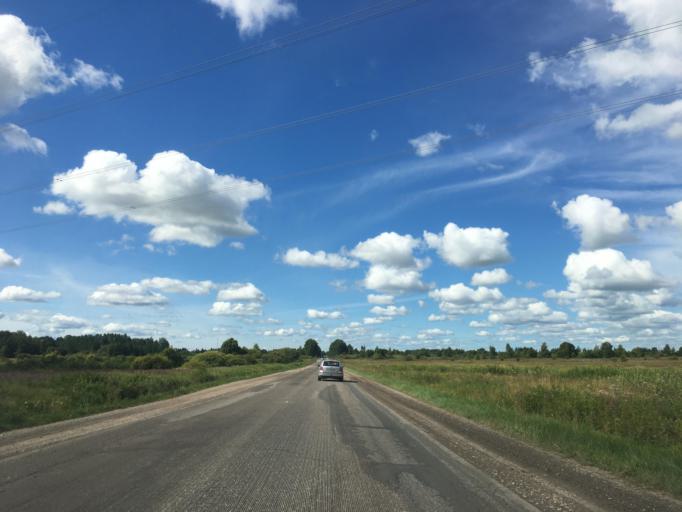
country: RU
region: Pskov
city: Palkino
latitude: 57.5494
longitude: 28.0425
